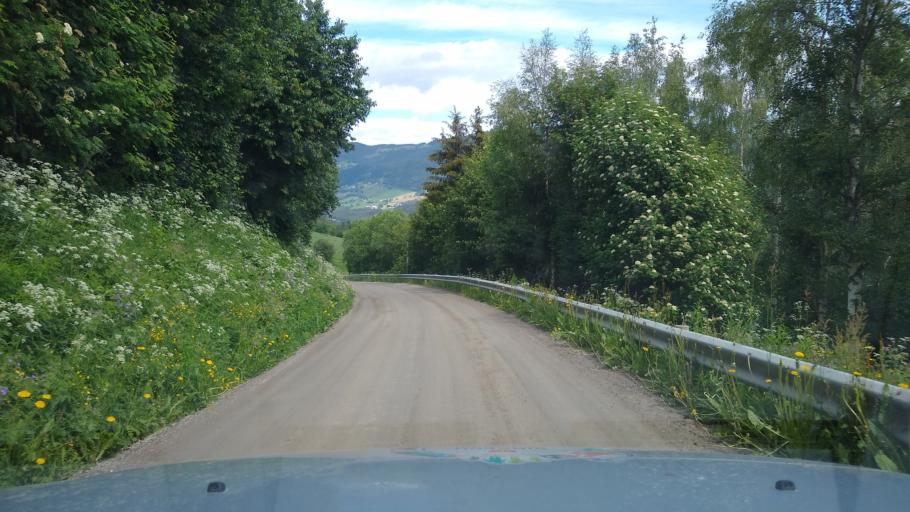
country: NO
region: Oppland
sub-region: Ringebu
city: Ringebu
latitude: 61.5118
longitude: 10.1339
